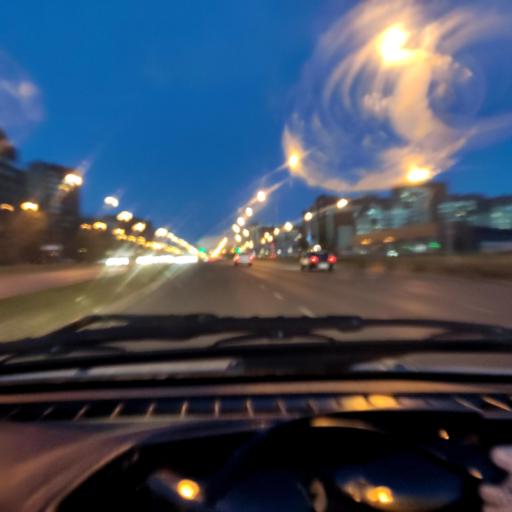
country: RU
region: Samara
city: Tol'yatti
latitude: 53.5347
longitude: 49.3494
